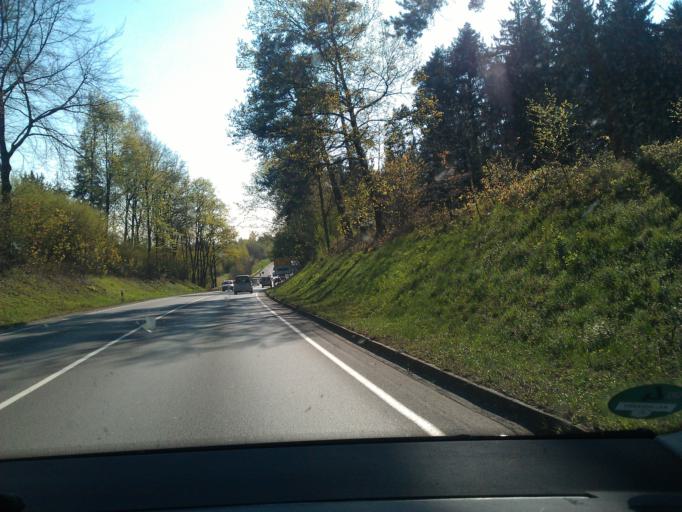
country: DE
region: Bavaria
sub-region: Swabia
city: Obergriesbach
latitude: 48.3999
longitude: 11.0797
